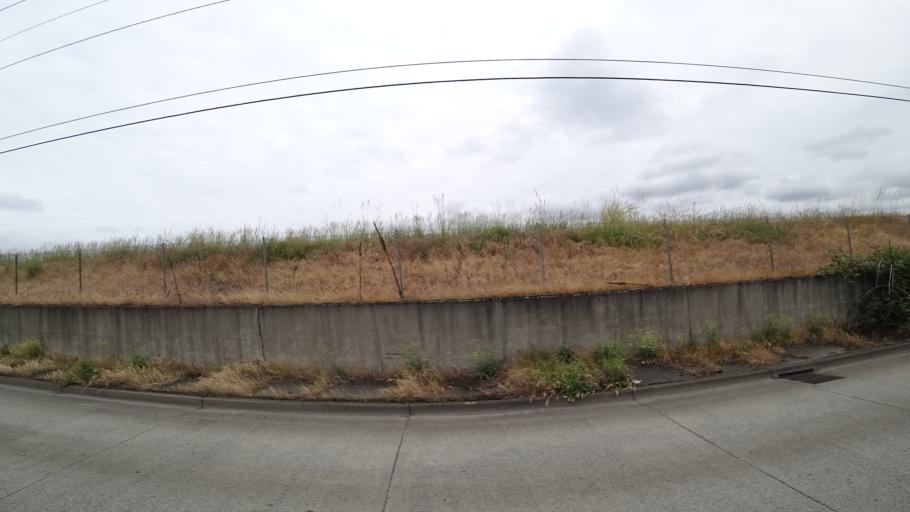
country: US
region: Washington
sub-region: Clark County
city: Vancouver
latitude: 45.6120
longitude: -122.7005
